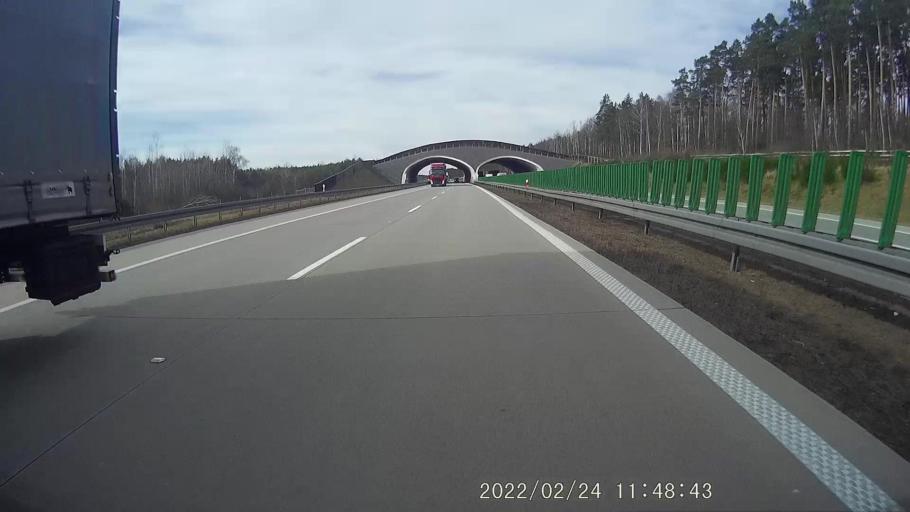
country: PL
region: Lower Silesian Voivodeship
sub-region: Powiat polkowicki
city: Radwanice
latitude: 51.5865
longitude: 15.9577
